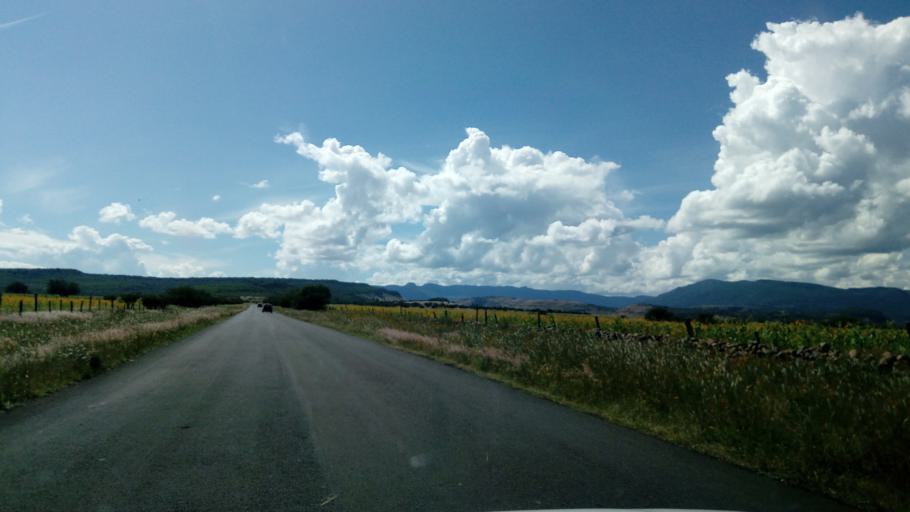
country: MX
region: Durango
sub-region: Durango
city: Jose Refugio Salcido
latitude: 23.8615
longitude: -104.4742
